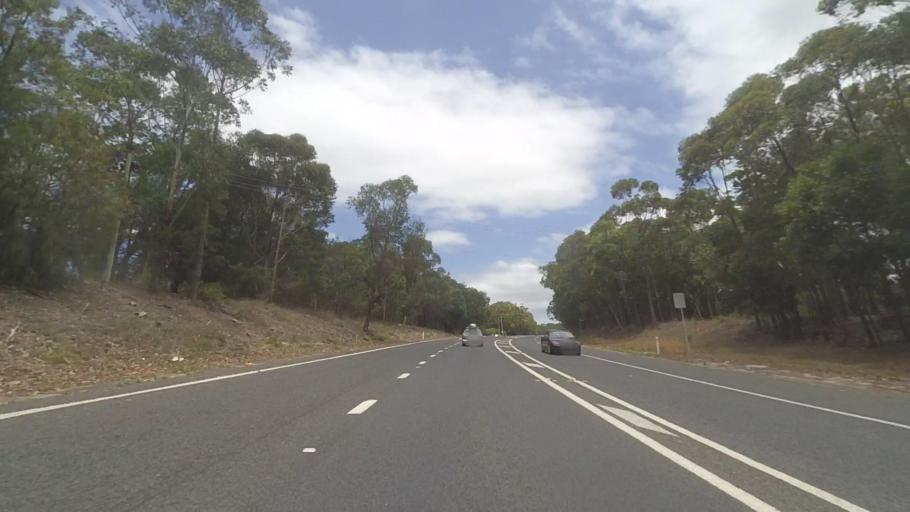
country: AU
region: New South Wales
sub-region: Shoalhaven Shire
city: Milton
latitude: -35.2299
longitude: 150.4347
